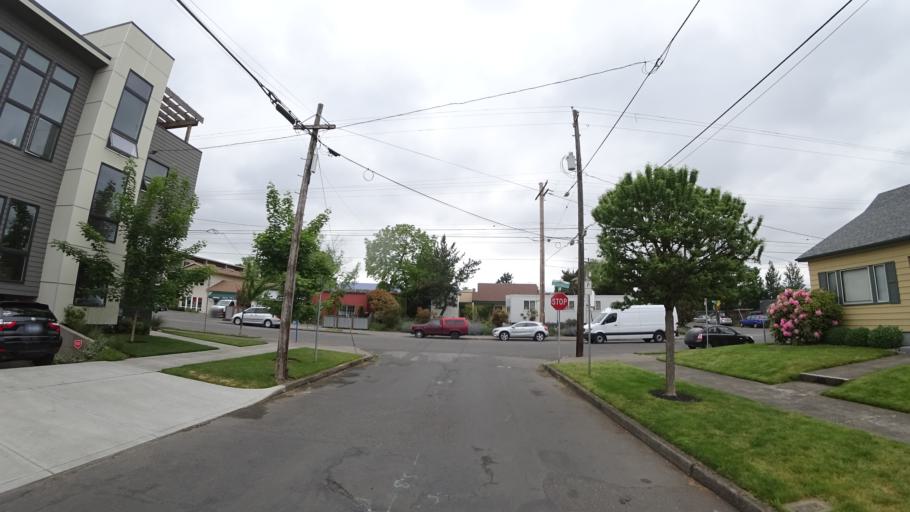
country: US
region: Oregon
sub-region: Multnomah County
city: Portland
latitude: 45.5480
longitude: -122.6105
